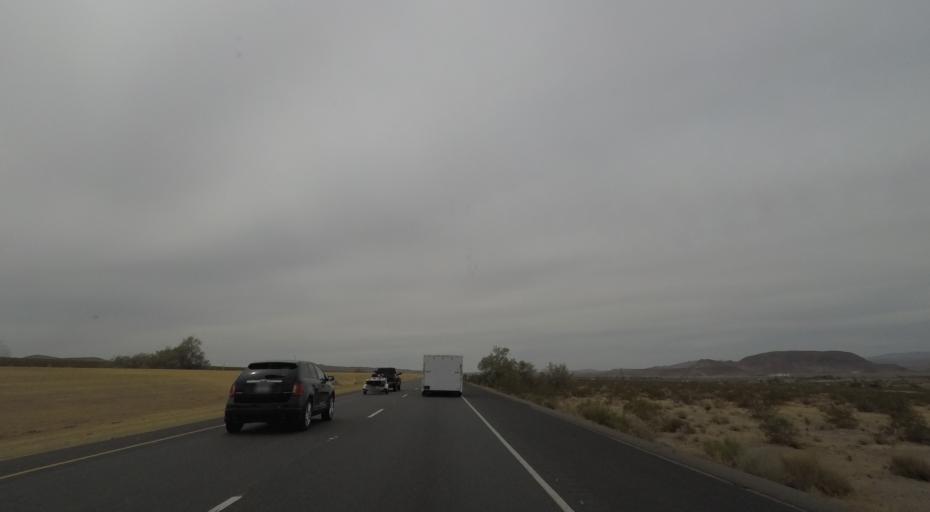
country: US
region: California
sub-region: San Bernardino County
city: Barstow
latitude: 34.8471
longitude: -116.8485
